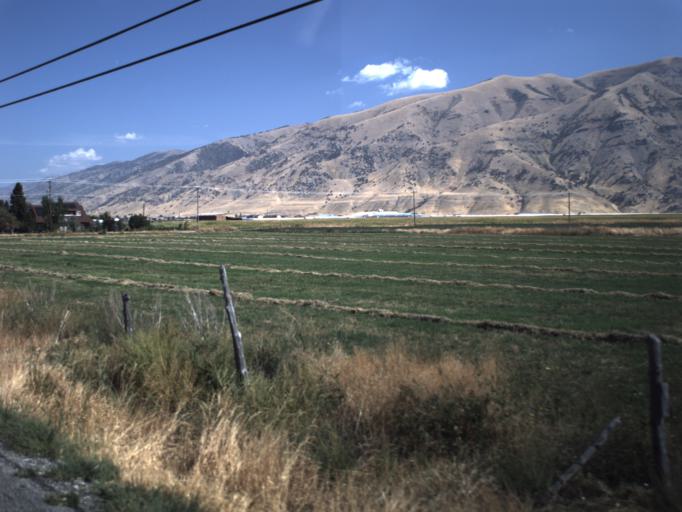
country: US
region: Utah
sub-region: Cache County
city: Hyrum
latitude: 41.6100
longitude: -111.8327
